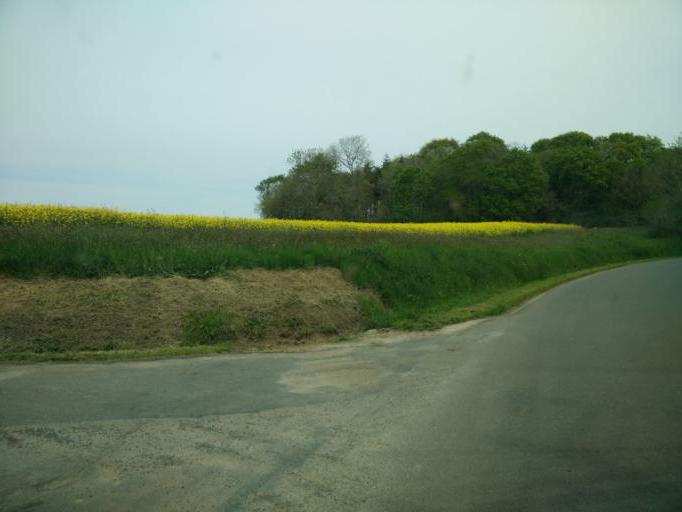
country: FR
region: Brittany
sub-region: Departement des Cotes-d'Armor
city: Plurien
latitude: 48.6504
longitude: -2.3525
